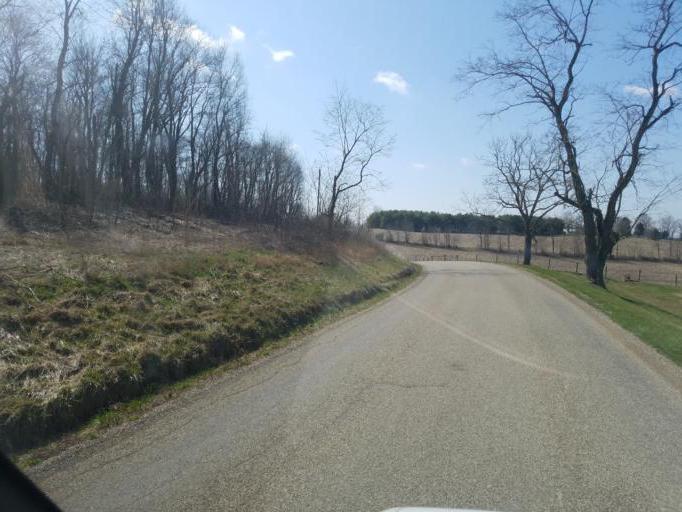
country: US
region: Ohio
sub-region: Licking County
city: Utica
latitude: 40.2532
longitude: -82.3377
